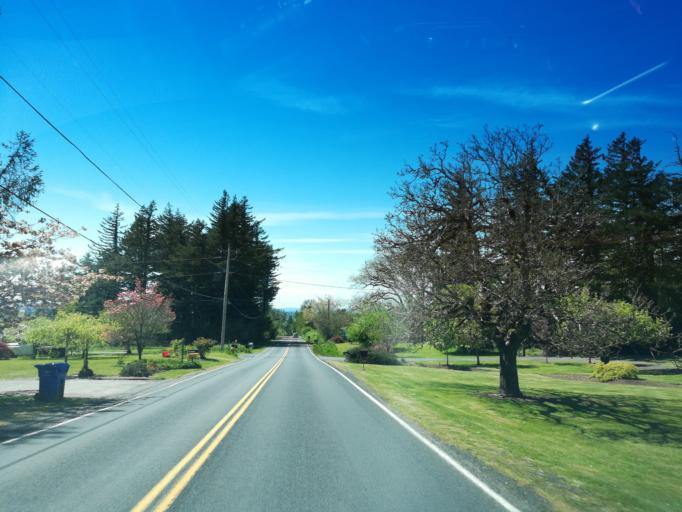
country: US
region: Oregon
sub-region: Multnomah County
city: Troutdale
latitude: 45.5227
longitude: -122.3565
